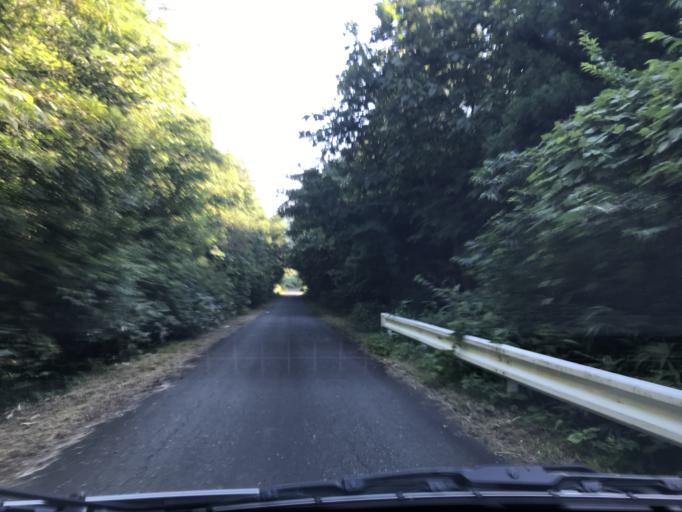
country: JP
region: Iwate
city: Mizusawa
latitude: 39.0633
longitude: 141.0409
